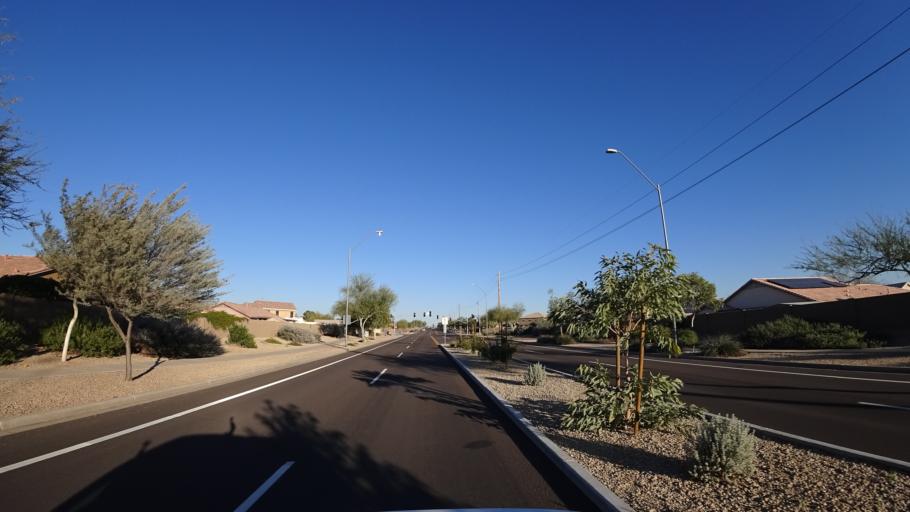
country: US
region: Arizona
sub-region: Maricopa County
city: Sun City West
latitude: 33.6818
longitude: -112.2911
